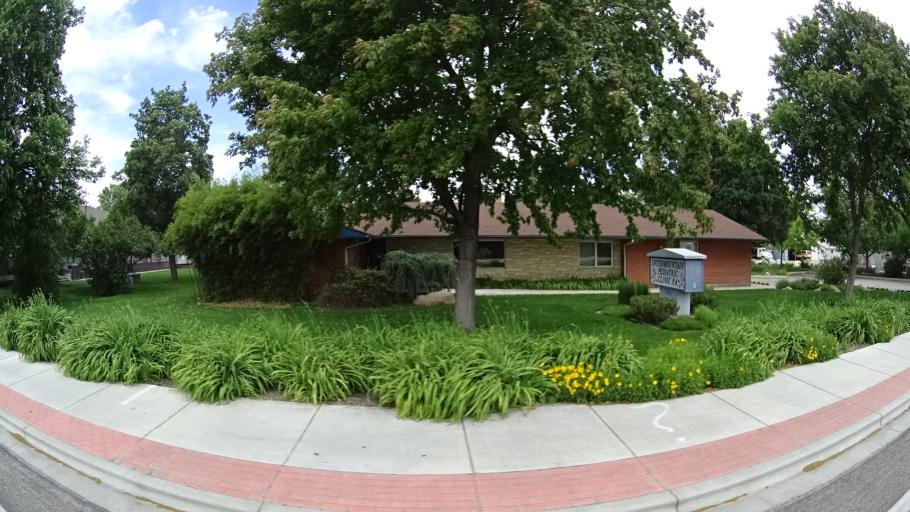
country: US
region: Idaho
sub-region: Ada County
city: Garden City
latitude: 43.6340
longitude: -116.2788
